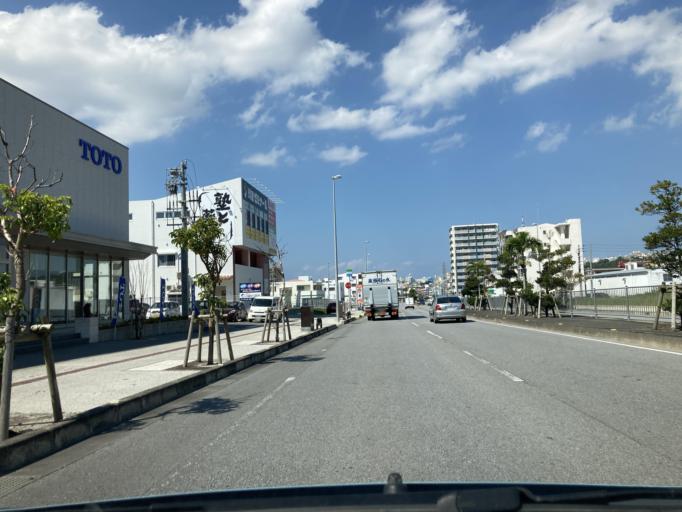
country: JP
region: Okinawa
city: Tomigusuku
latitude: 26.1896
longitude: 127.7169
